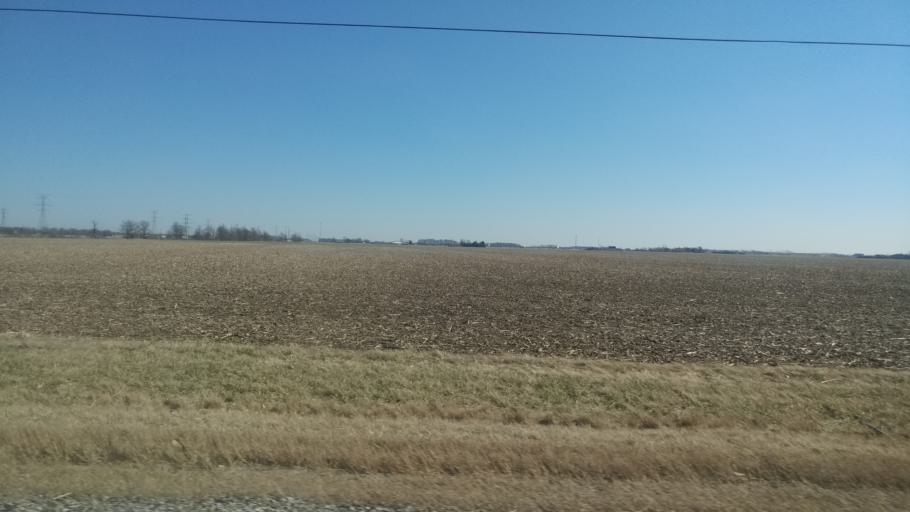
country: US
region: Ohio
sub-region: Wood County
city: Haskins
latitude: 41.4716
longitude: -83.6480
